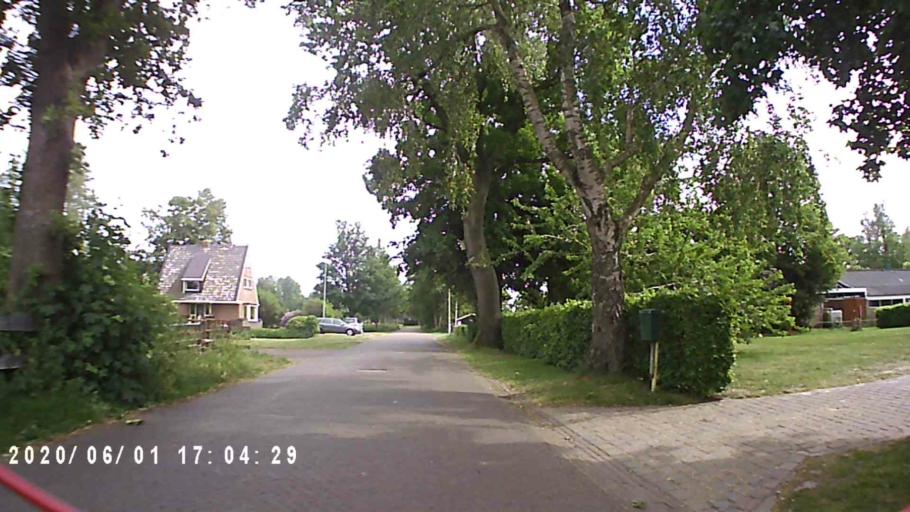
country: NL
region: Friesland
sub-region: Gemeente Tytsjerksteradiel
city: Garyp
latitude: 53.1741
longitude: 5.9335
